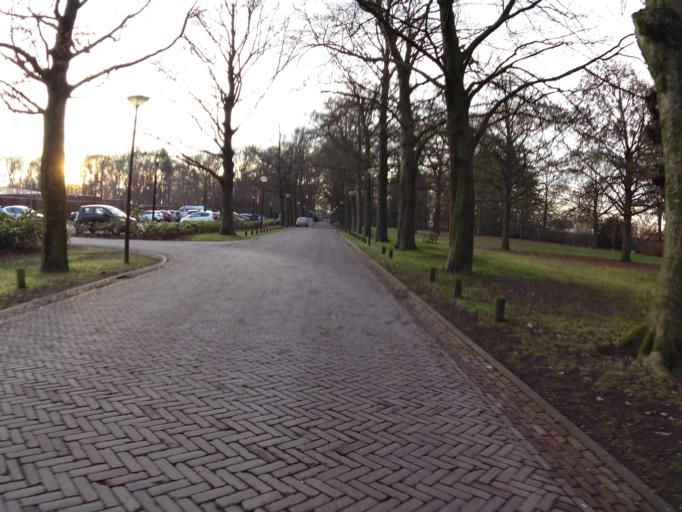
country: NL
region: North Brabant
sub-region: Gemeente Vught
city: Vught
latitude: 51.6406
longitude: 5.3011
